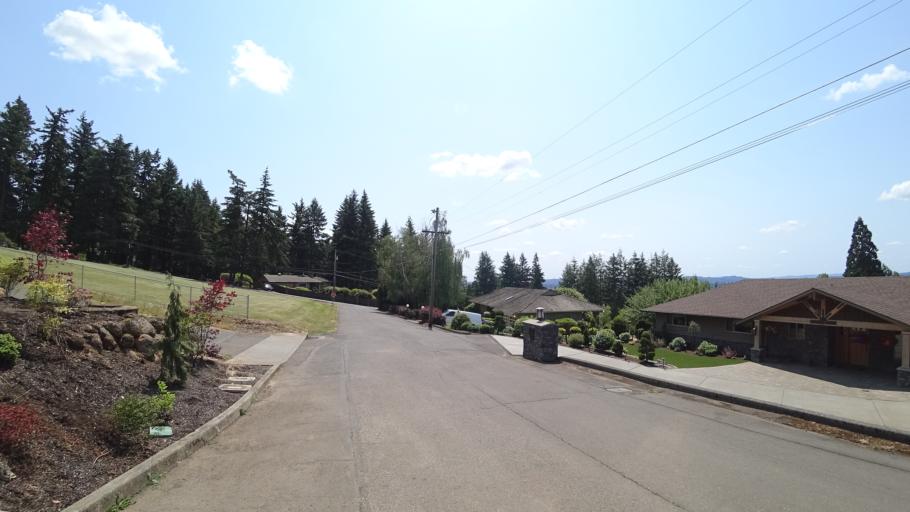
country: US
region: Oregon
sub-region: Multnomah County
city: Lents
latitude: 45.4512
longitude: -122.5635
